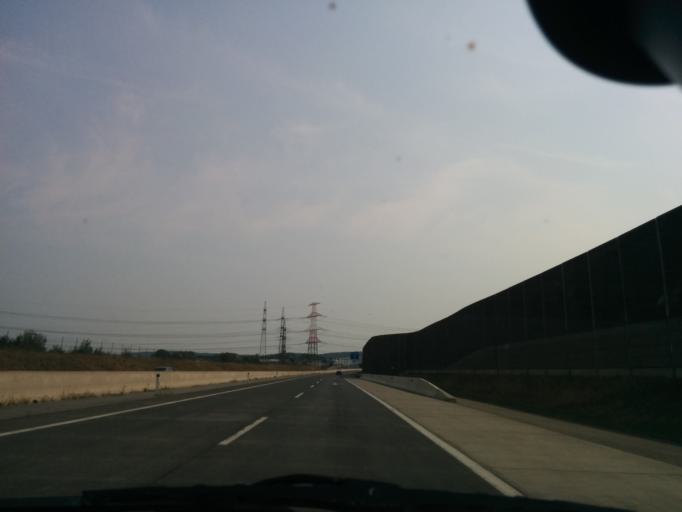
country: AT
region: Lower Austria
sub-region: Politischer Bezirk Korneuburg
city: Korneuburg
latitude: 48.3633
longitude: 16.3445
